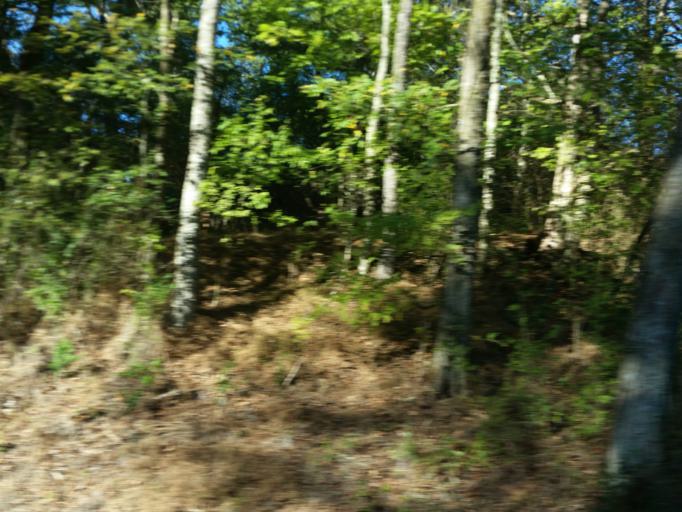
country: US
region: Tennessee
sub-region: Grainger County
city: Rutledge
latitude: 36.2394
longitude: -83.6179
